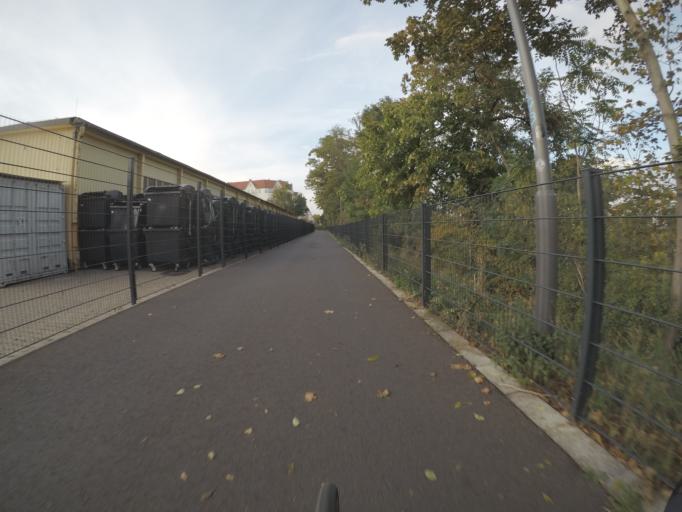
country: DE
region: Berlin
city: Berlin Schoeneberg
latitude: 52.4870
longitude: 13.3706
